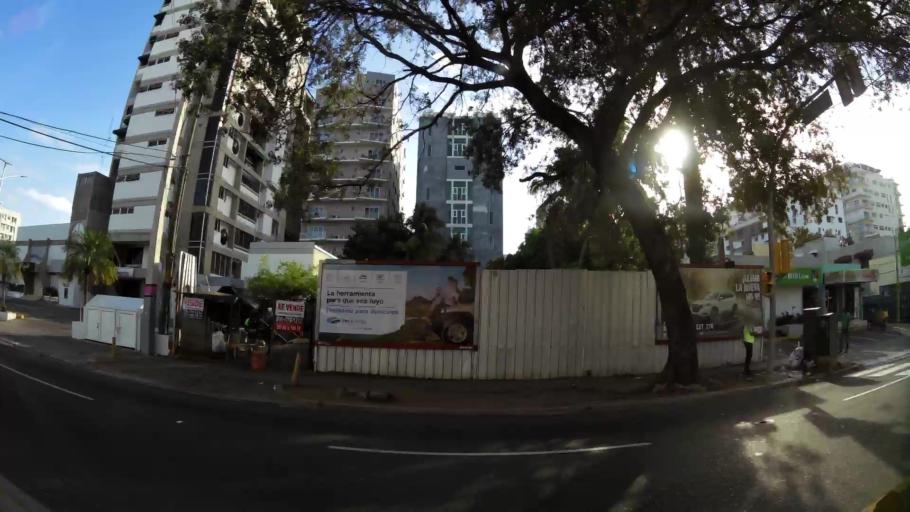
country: DO
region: Nacional
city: La Julia
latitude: 18.4745
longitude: -69.9263
